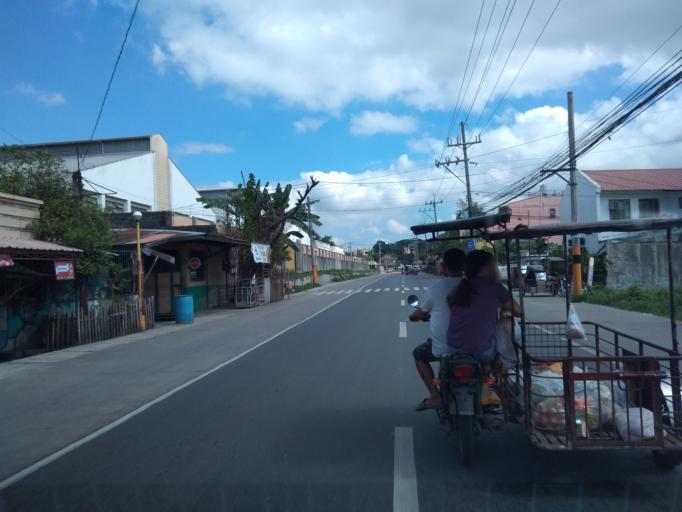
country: PH
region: Central Luzon
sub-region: Province of Bulacan
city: Guyong
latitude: 14.8322
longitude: 120.9741
